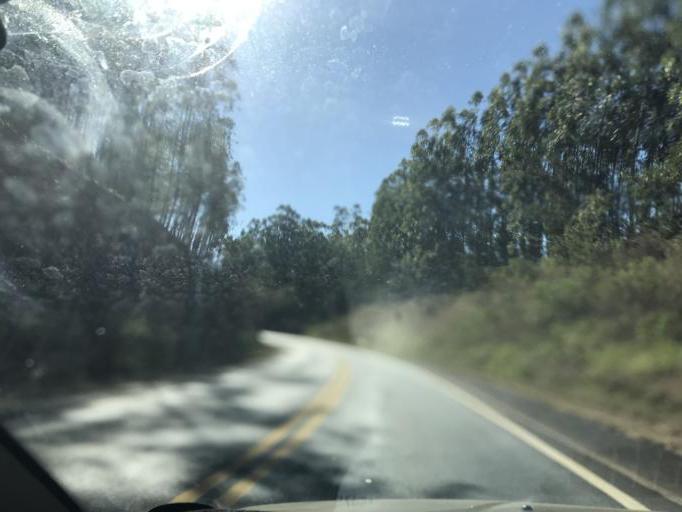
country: BR
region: Minas Gerais
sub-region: Bambui
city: Bambui
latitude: -19.8256
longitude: -46.0096
